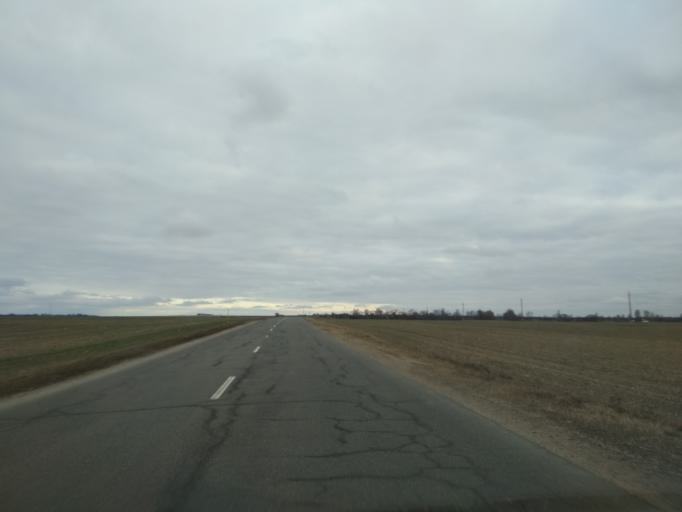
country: BY
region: Minsk
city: Mar''ina Horka
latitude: 53.5581
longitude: 28.0656
